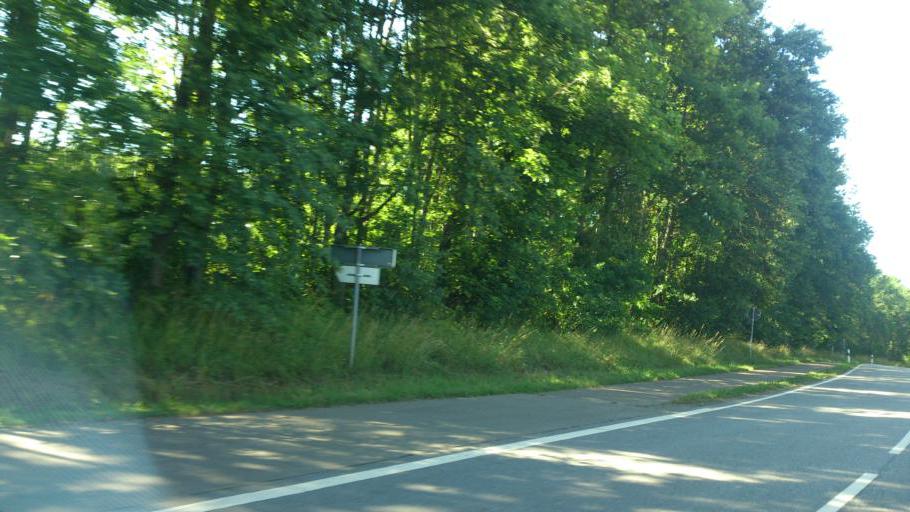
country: DE
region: Saarland
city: Oberthal
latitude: 49.5613
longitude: 7.0614
